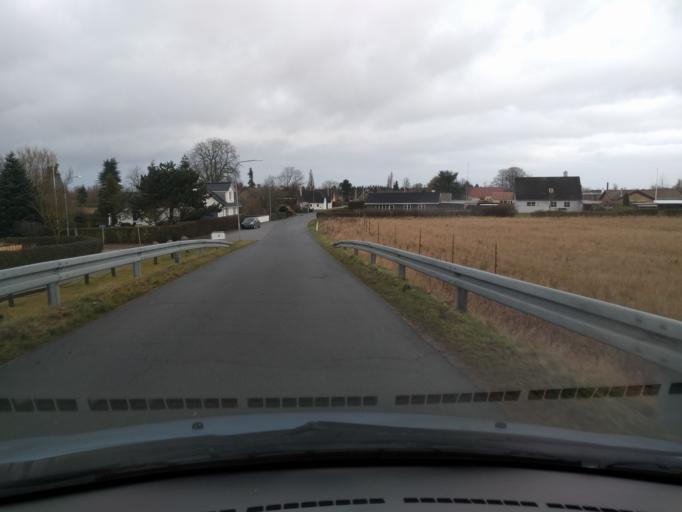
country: DK
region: South Denmark
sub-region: Kerteminde Kommune
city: Langeskov
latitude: 55.3674
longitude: 10.5639
